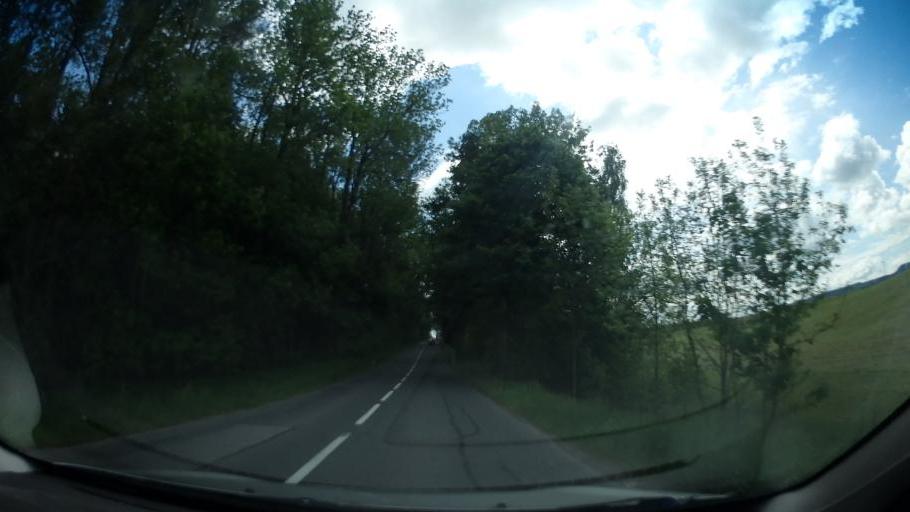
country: CZ
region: Pardubicky
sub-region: Okres Svitavy
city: Moravska Trebova
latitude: 49.7273
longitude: 16.6417
